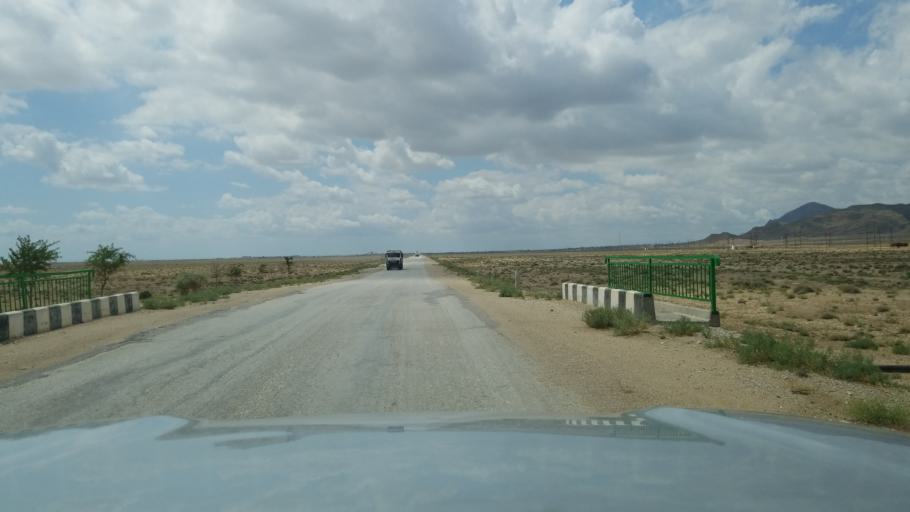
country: TM
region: Balkan
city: Balkanabat
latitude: 39.4813
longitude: 54.4492
